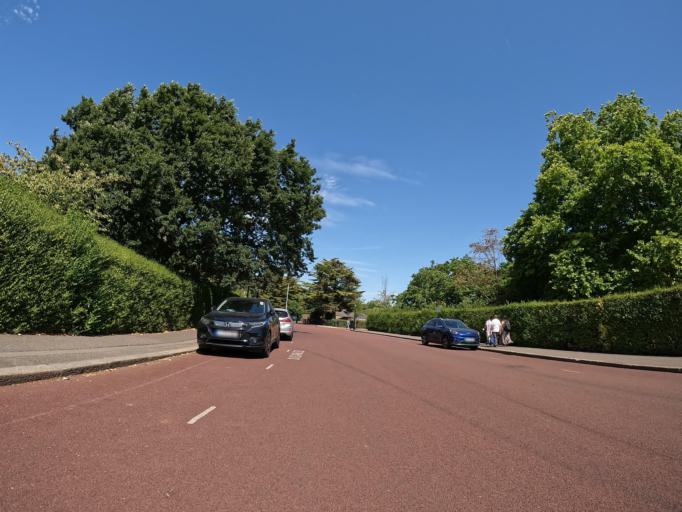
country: GB
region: England
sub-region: Greater London
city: Camden Town
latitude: 51.5274
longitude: -0.1512
